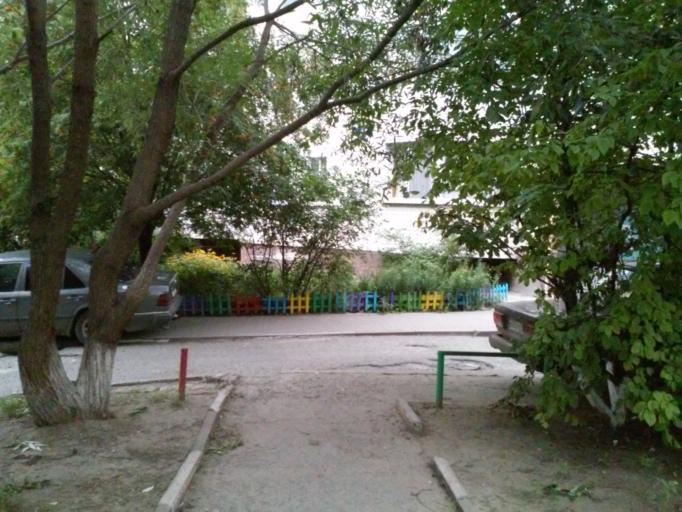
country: RU
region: Belgorod
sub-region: Belgorodskiy Rayon
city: Belgorod
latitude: 50.5675
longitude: 36.5757
